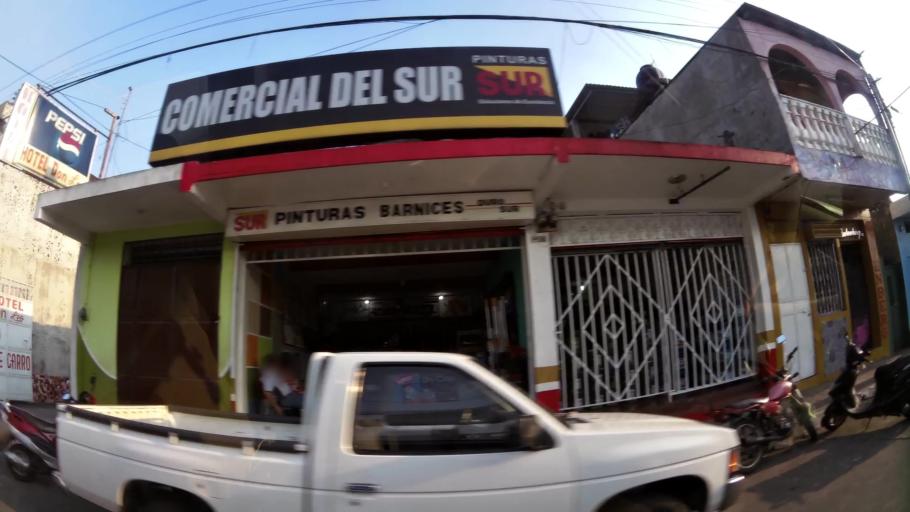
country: GT
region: Retalhuleu
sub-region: Municipio de Retalhuleu
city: Retalhuleu
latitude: 14.5351
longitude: -91.6811
